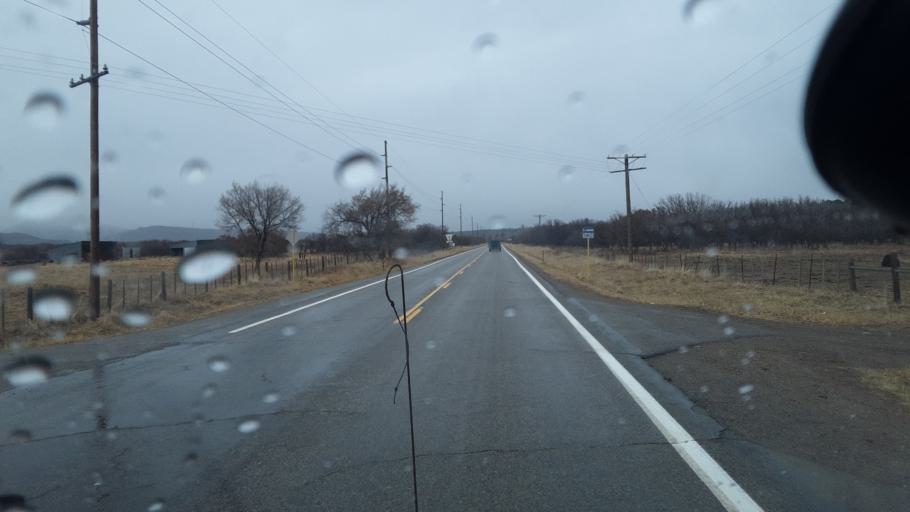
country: US
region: Colorado
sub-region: La Plata County
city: Durango
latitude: 37.2315
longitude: -108.0475
